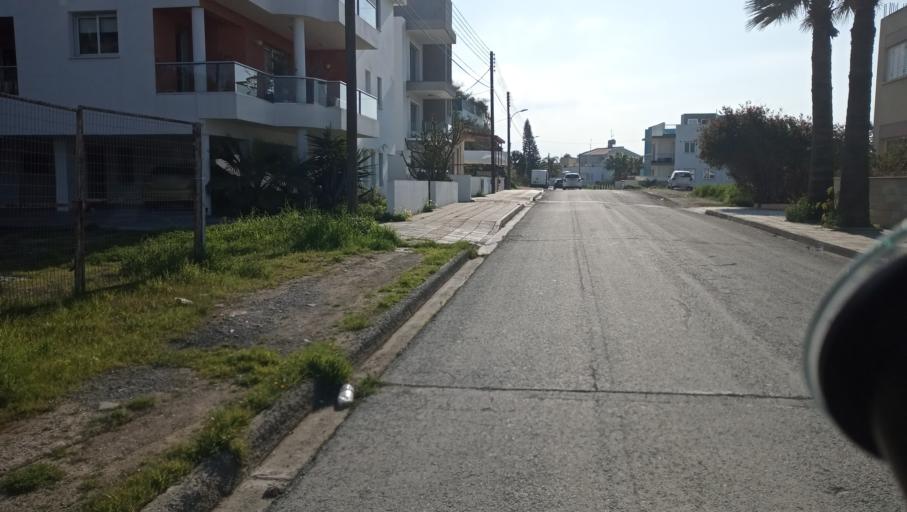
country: CY
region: Lefkosia
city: Nicosia
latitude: 35.1468
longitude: 33.3184
